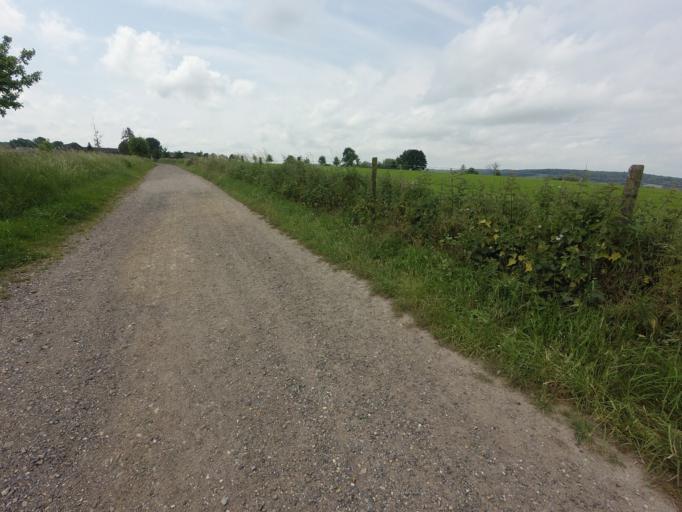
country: NL
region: Limburg
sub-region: Gemeente Simpelveld
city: Simpelveld
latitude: 50.7930
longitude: 5.9403
